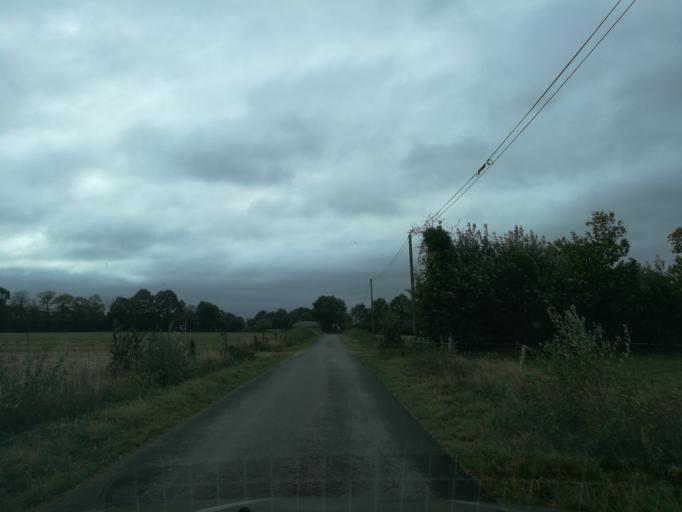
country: FR
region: Brittany
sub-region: Departement d'Ille-et-Vilaine
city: Pleumeleuc
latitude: 48.1749
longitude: -1.9255
